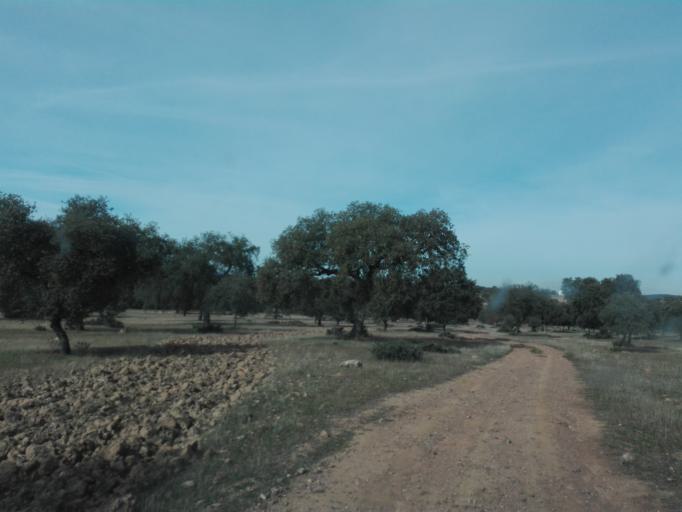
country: ES
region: Extremadura
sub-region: Provincia de Badajoz
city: Campillo de Llerena
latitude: 38.4675
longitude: -5.8877
